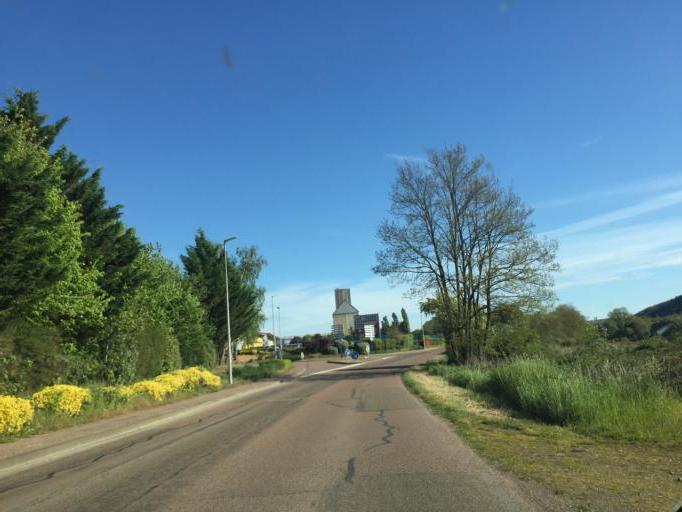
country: FR
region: Bourgogne
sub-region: Departement de la Nievre
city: Clamecy
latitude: 47.4677
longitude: 3.5200
